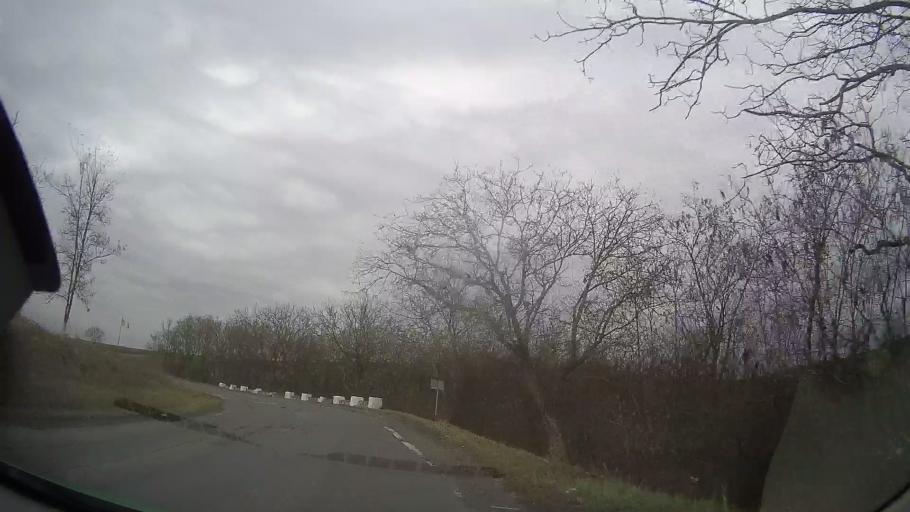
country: RO
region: Mures
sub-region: Comuna Faragau
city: Faragau
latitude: 46.7634
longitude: 24.5295
